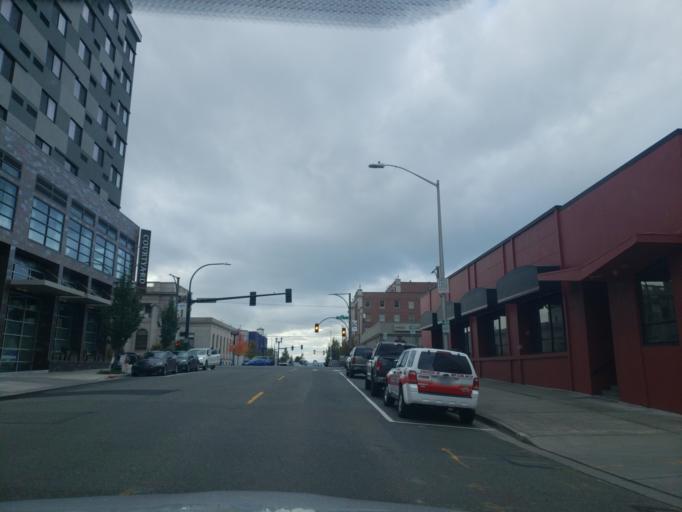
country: US
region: Washington
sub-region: Snohomish County
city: Everett
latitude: 47.9779
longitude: -122.2078
